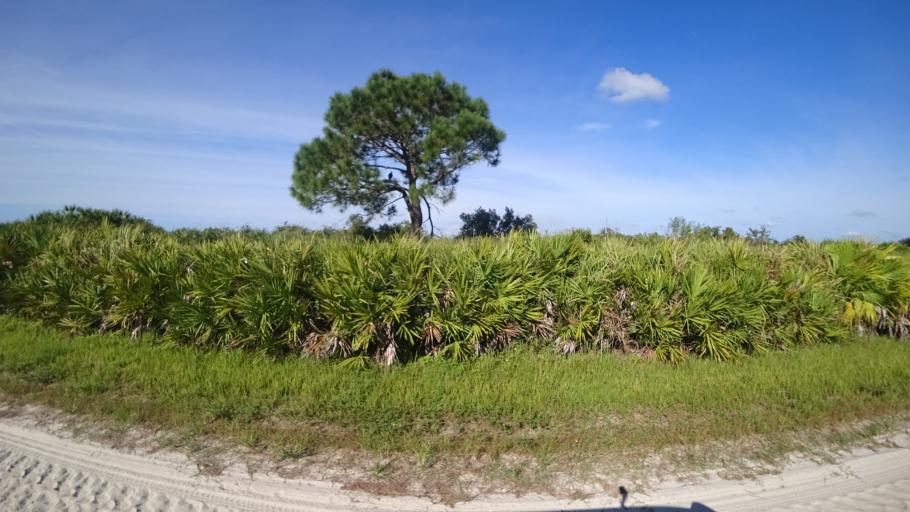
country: US
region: Florida
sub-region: Sarasota County
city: The Meadows
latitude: 27.4526
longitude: -82.3372
